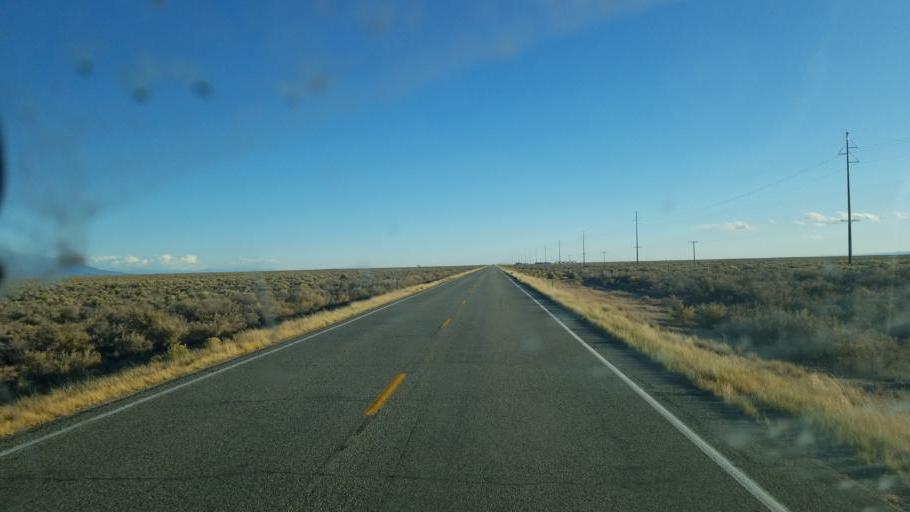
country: US
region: Colorado
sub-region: Saguache County
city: Saguache
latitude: 37.9630
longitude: -105.9046
